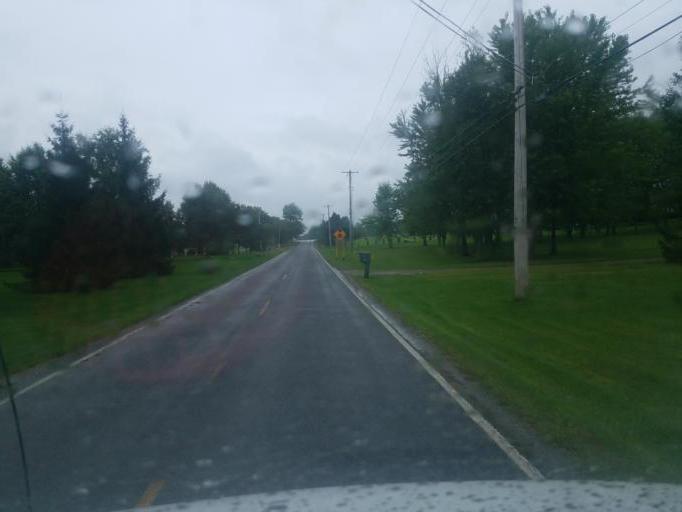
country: US
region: Ohio
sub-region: Medina County
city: Seville
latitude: 41.0226
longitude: -81.8149
